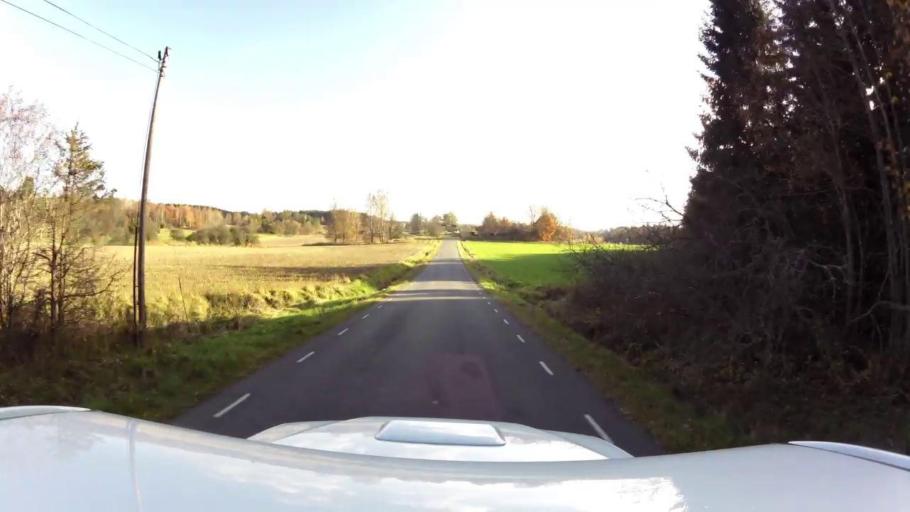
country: SE
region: OEstergoetland
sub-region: Linkopings Kommun
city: Vikingstad
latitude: 58.2594
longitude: 15.4589
